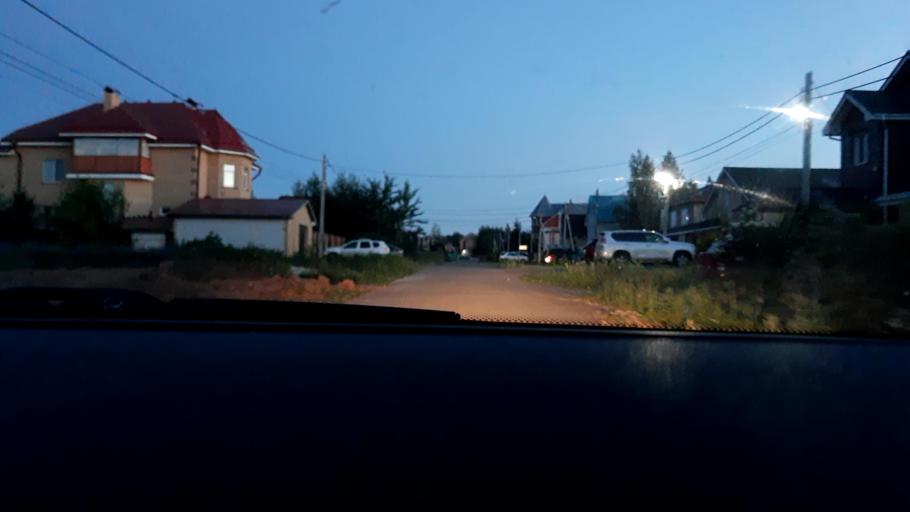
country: RU
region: Nizjnij Novgorod
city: Nizhniy Novgorod
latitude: 56.2170
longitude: 43.9555
